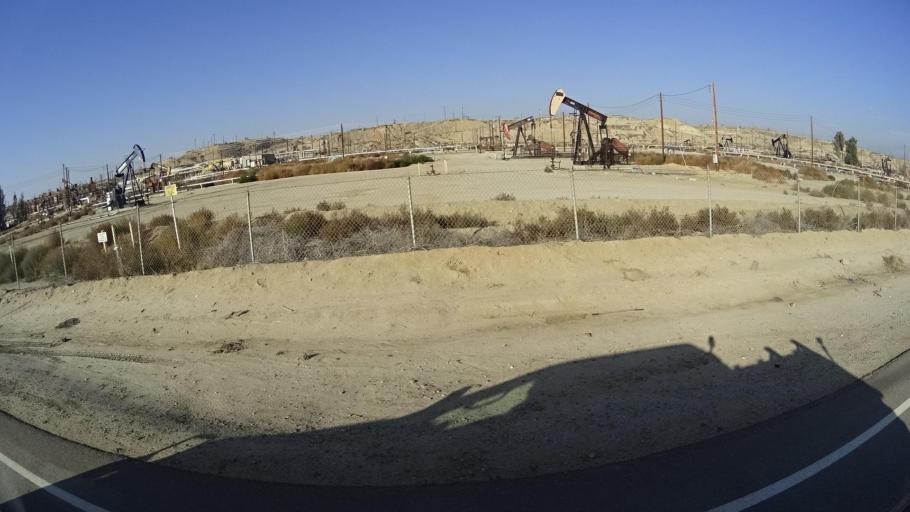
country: US
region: California
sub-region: Kern County
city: Oildale
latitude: 35.4277
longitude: -118.9660
